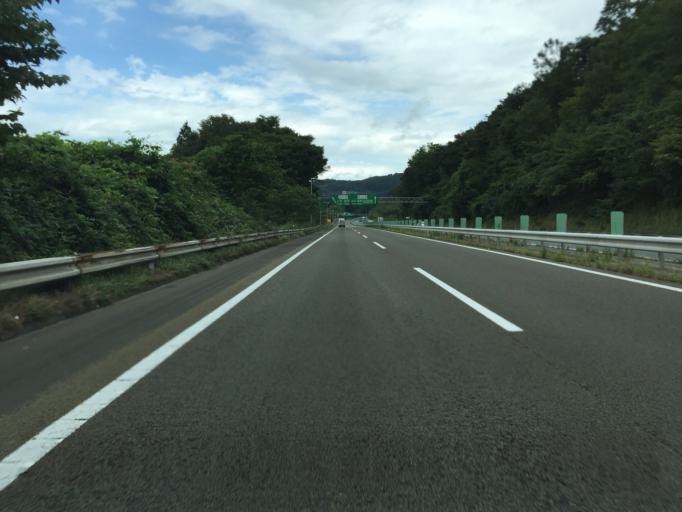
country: JP
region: Miyagi
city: Okawara
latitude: 38.1289
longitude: 140.7187
